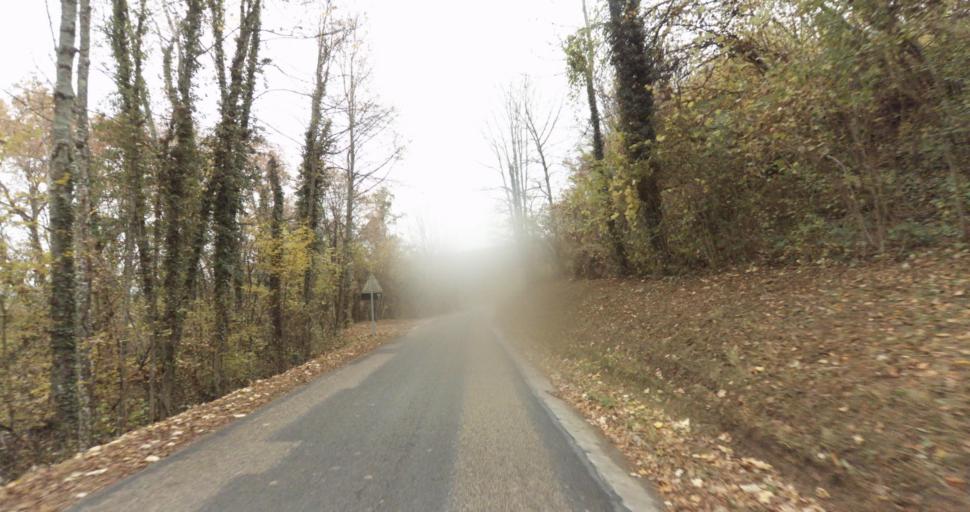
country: FR
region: Rhone-Alpes
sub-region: Departement de la Savoie
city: Albens
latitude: 45.7601
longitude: 5.9621
